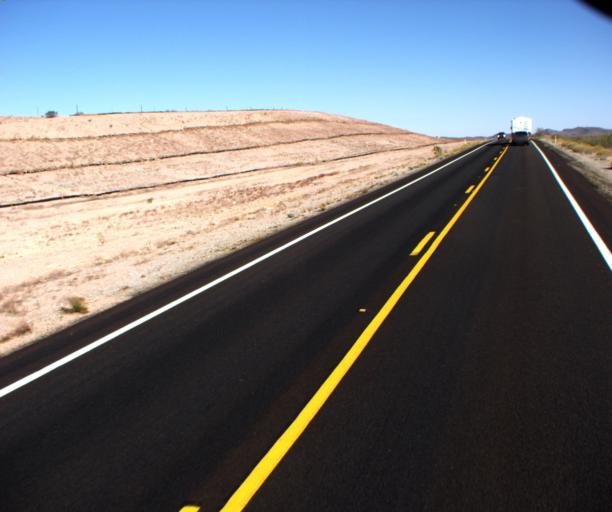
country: US
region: Arizona
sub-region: La Paz County
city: Quartzsite
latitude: 33.1723
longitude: -114.2766
